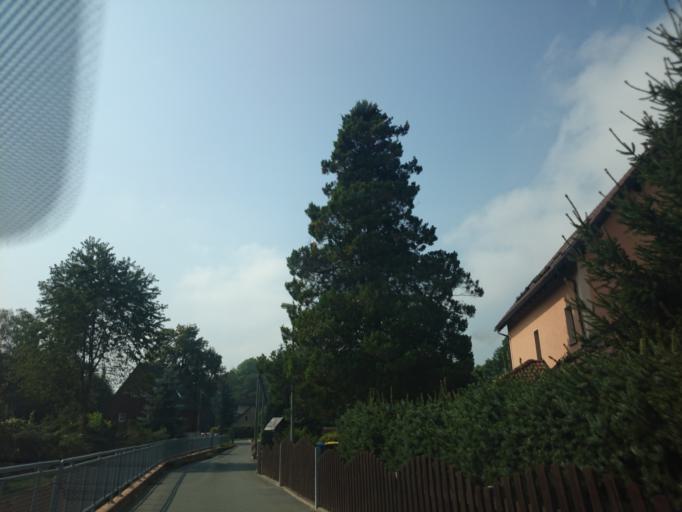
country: DE
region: Saxony
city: Brand-Erbisdorf
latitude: 50.8684
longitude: 13.3117
